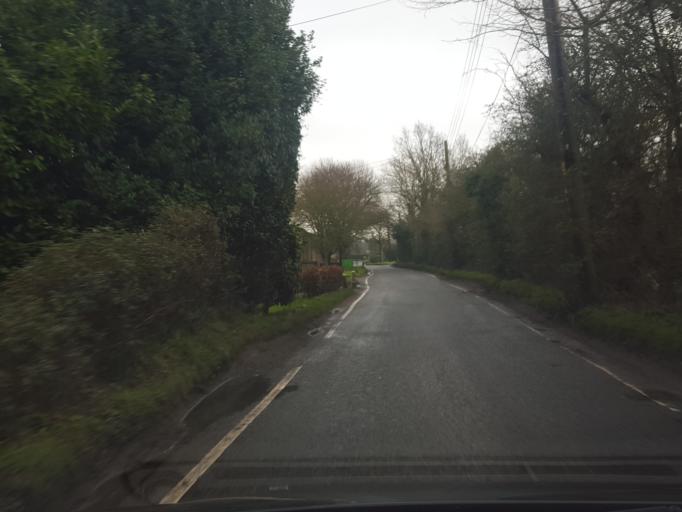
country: GB
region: England
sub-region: Essex
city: Great Horkesley
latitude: 51.9444
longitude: 0.8782
